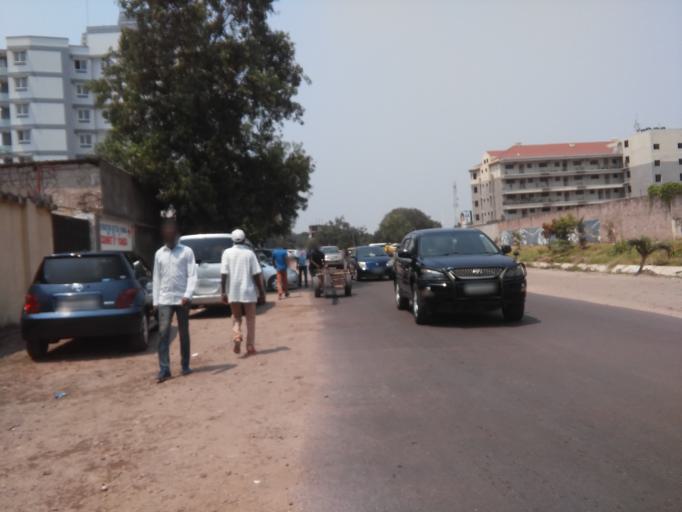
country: CD
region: Kinshasa
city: Kinshasa
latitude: -4.3173
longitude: 15.2907
